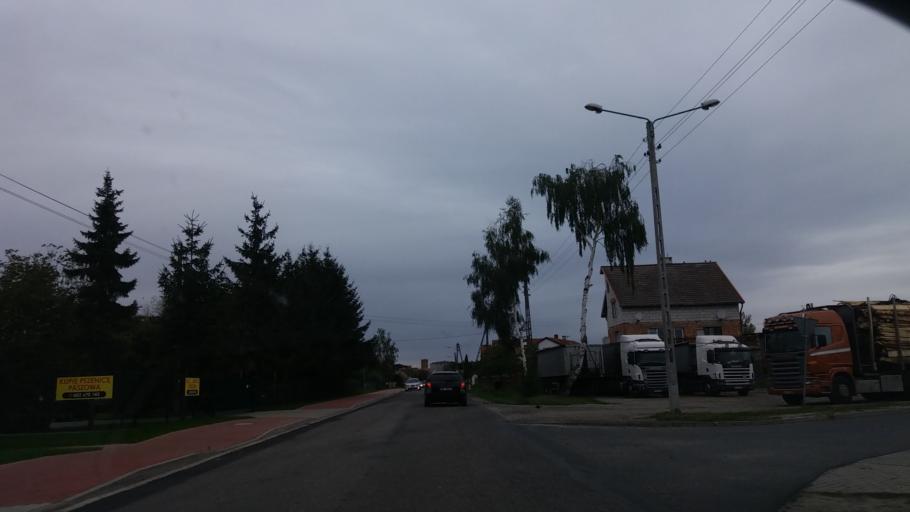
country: PL
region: Lower Silesian Voivodeship
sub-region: Powiat legnicki
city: Prochowice
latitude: 51.2676
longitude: 16.3656
